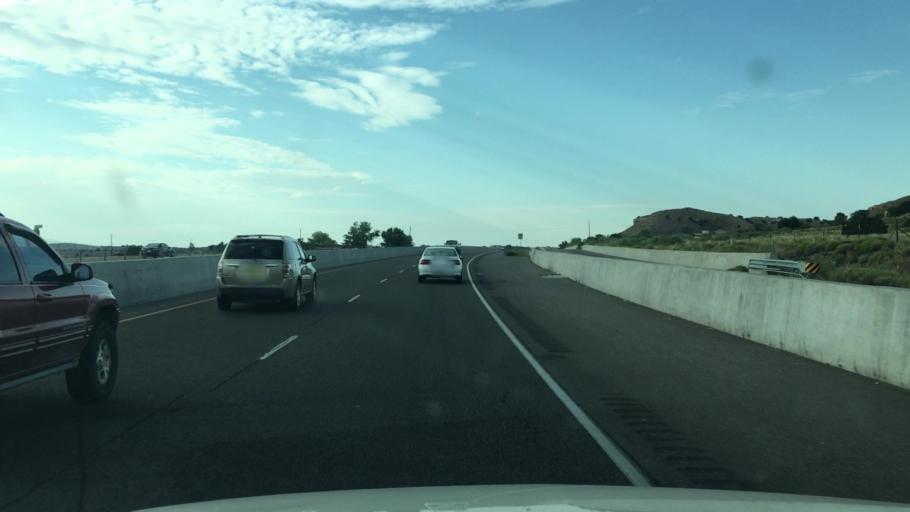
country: US
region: New Mexico
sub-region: Santa Fe County
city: El Valle de Arroyo Seco
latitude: 35.9532
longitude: -106.0212
